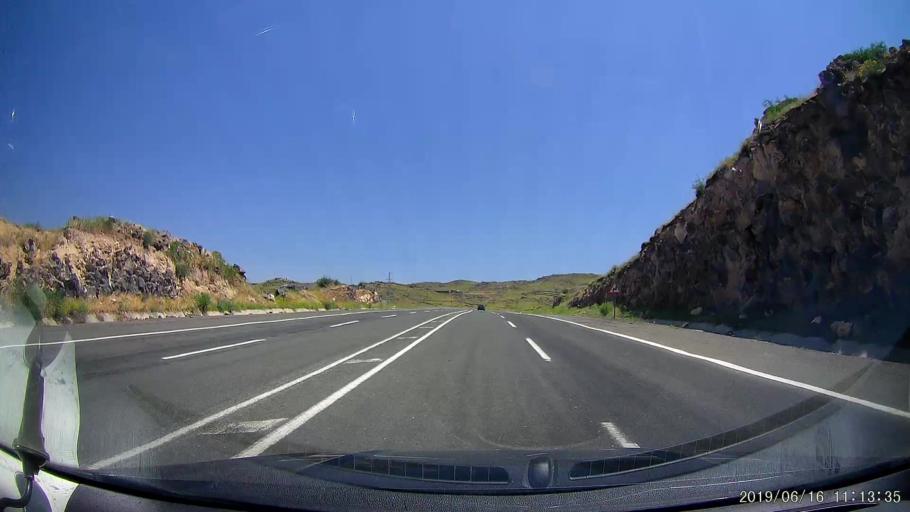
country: TR
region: Igdir
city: Igdir
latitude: 39.7849
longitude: 44.1405
